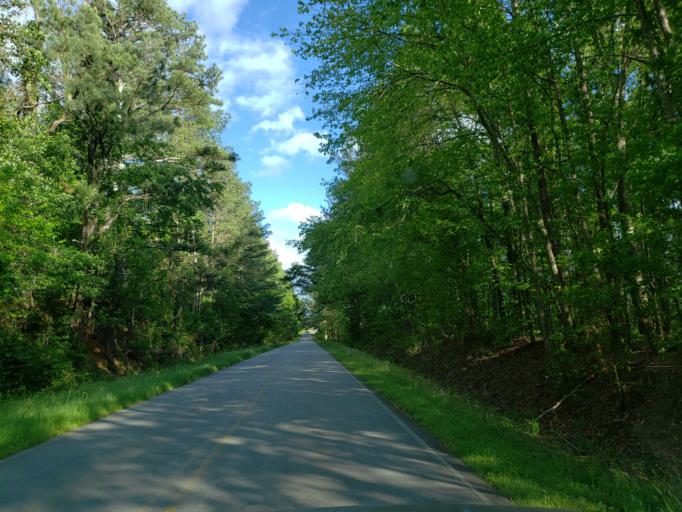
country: US
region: Georgia
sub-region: Haralson County
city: Tallapoosa
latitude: 33.7762
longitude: -85.3083
